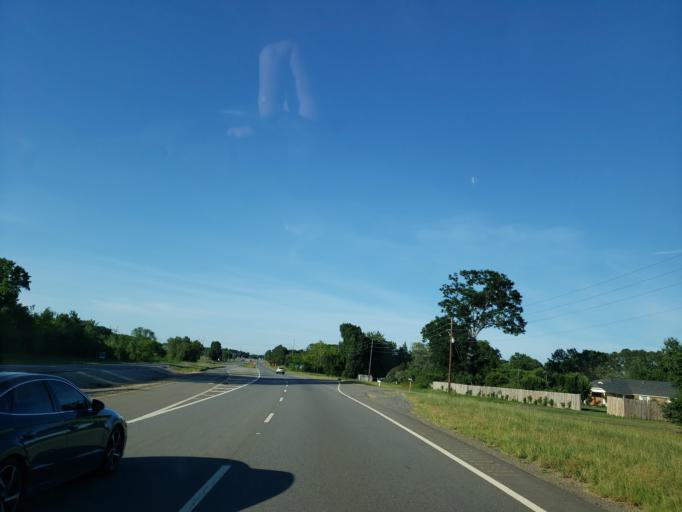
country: US
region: Georgia
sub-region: Floyd County
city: Shannon
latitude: 34.3591
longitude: -85.0568
